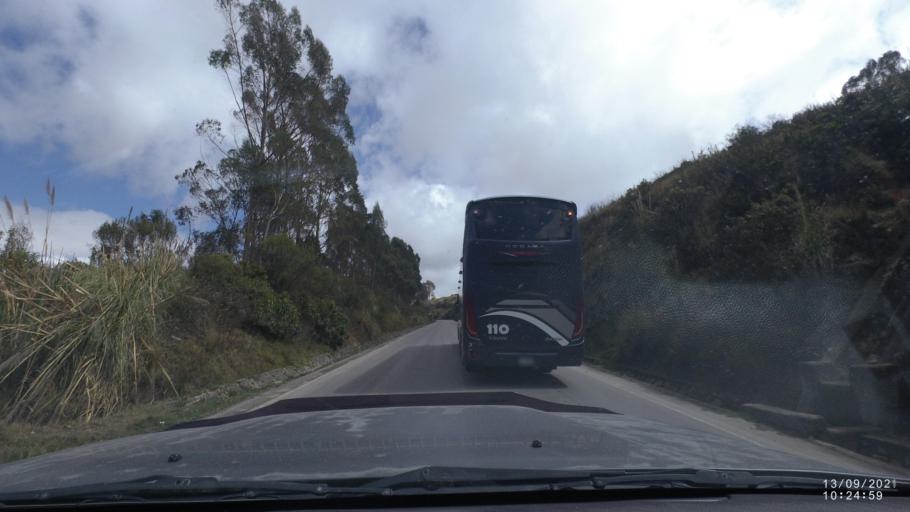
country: BO
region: Cochabamba
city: Colomi
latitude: -17.3149
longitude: -65.8618
